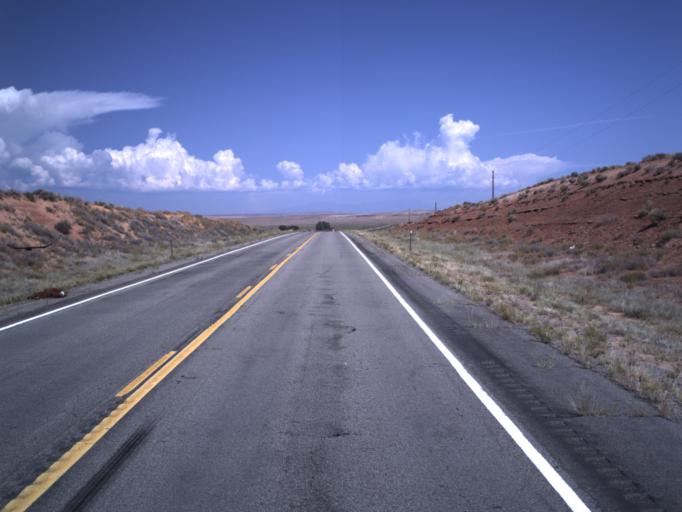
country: US
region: Utah
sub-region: San Juan County
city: Blanding
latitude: 37.0865
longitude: -109.5479
